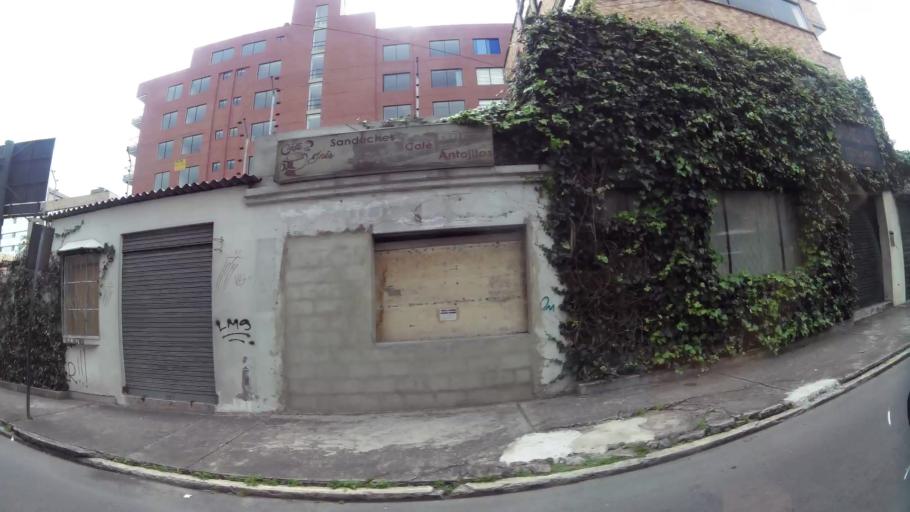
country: EC
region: Pichincha
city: Quito
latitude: -0.2082
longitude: -78.4855
